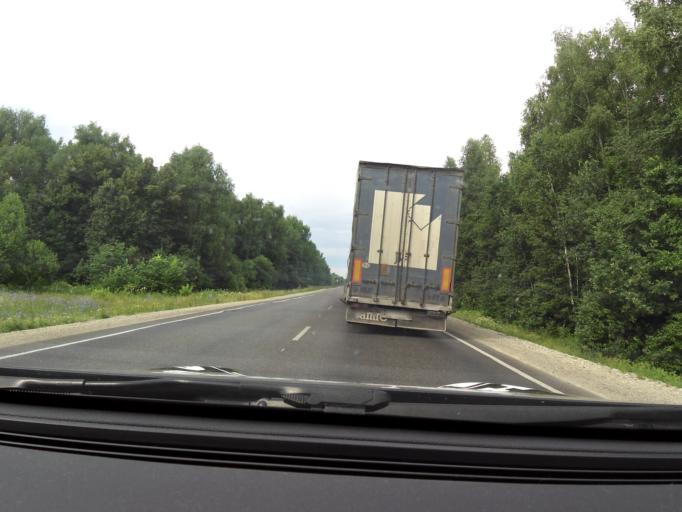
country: RU
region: Bashkortostan
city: Ulu-Telyak
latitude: 54.8525
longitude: 57.1247
